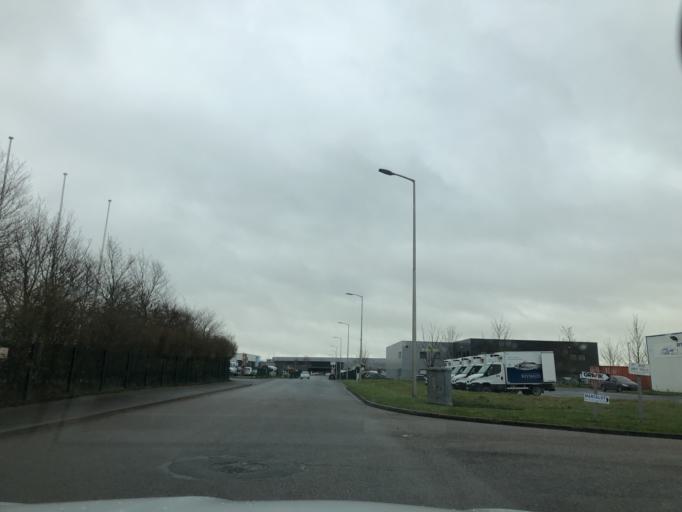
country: FR
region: Lower Normandy
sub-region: Departement du Calvados
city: Giberville
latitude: 49.1714
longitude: -0.2946
